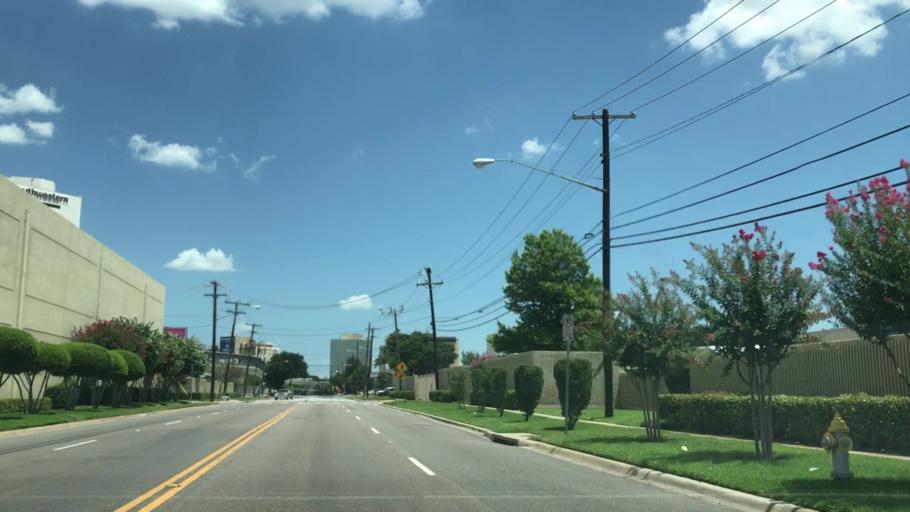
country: US
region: Texas
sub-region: Dallas County
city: Dallas
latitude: 32.8176
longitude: -96.8523
